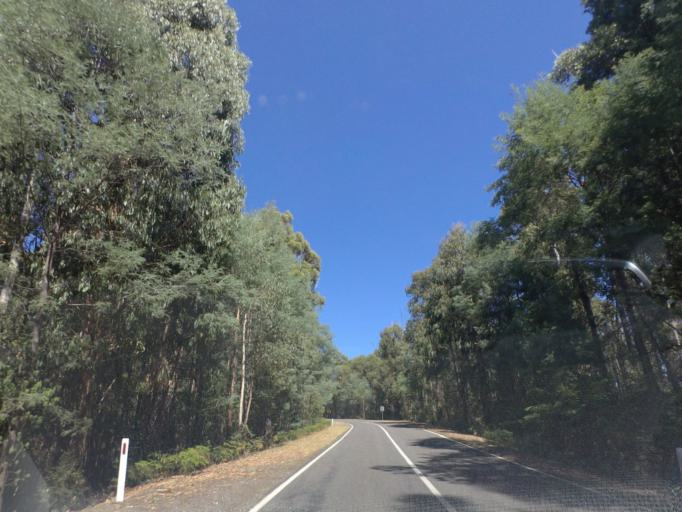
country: AU
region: Victoria
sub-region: Yarra Ranges
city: Millgrove
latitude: -37.5108
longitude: 145.7674
